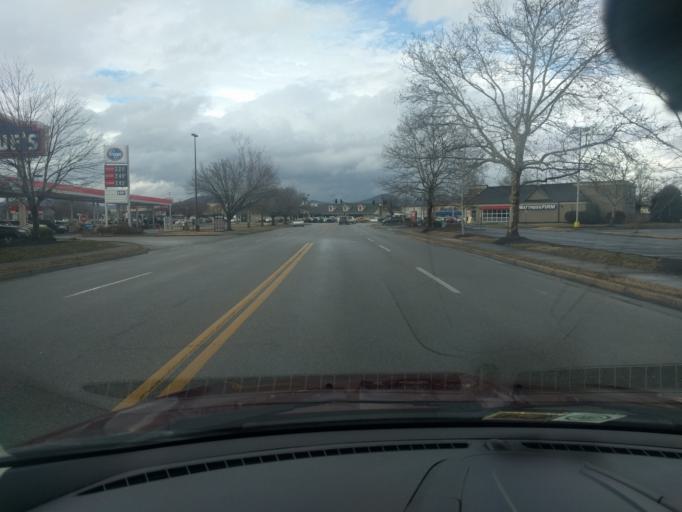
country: US
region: Virginia
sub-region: Roanoke County
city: Hollins
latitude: 37.3174
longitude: -79.9633
